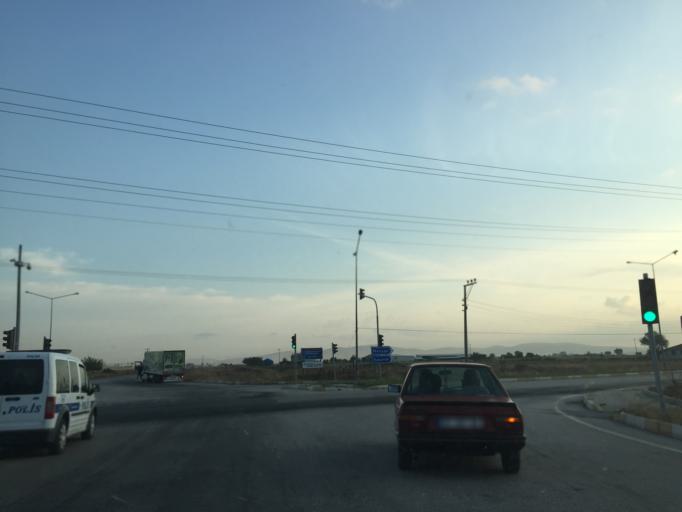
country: TR
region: Balikesir
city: Gonen
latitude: 40.1035
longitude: 27.6760
